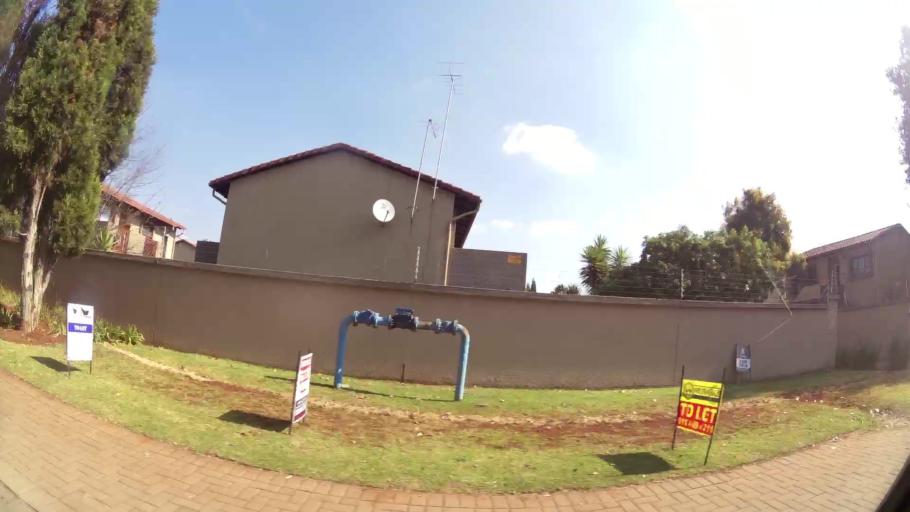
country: ZA
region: Gauteng
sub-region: Ekurhuleni Metropolitan Municipality
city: Boksburg
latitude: -26.1953
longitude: 28.2860
